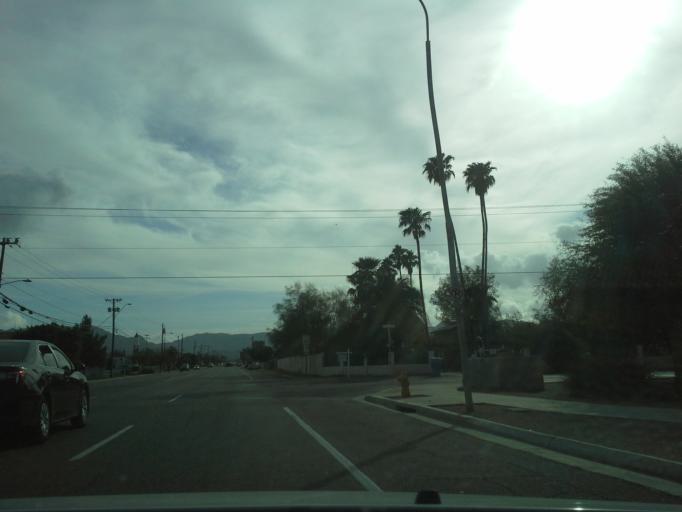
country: US
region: Arizona
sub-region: Maricopa County
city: Phoenix
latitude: 33.3963
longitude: -112.0820
